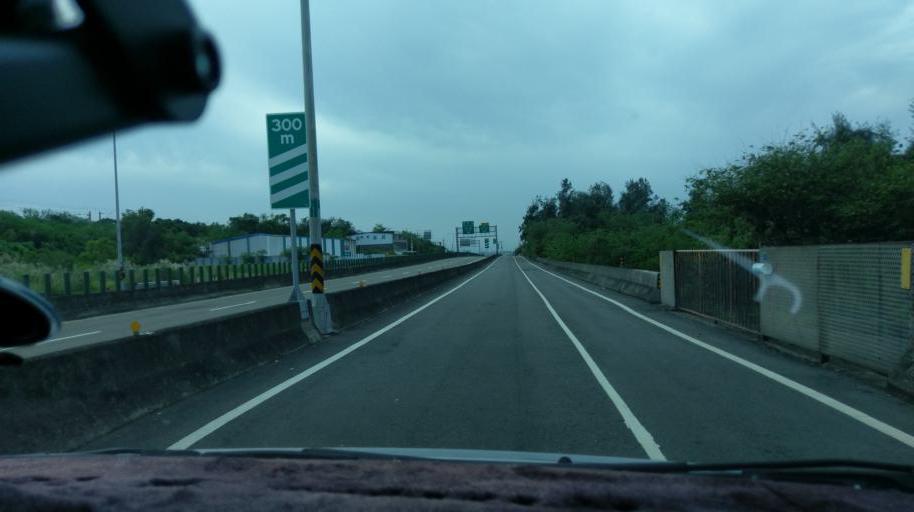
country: TW
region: Taiwan
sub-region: Hsinchu
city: Hsinchu
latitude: 24.7195
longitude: 120.8680
